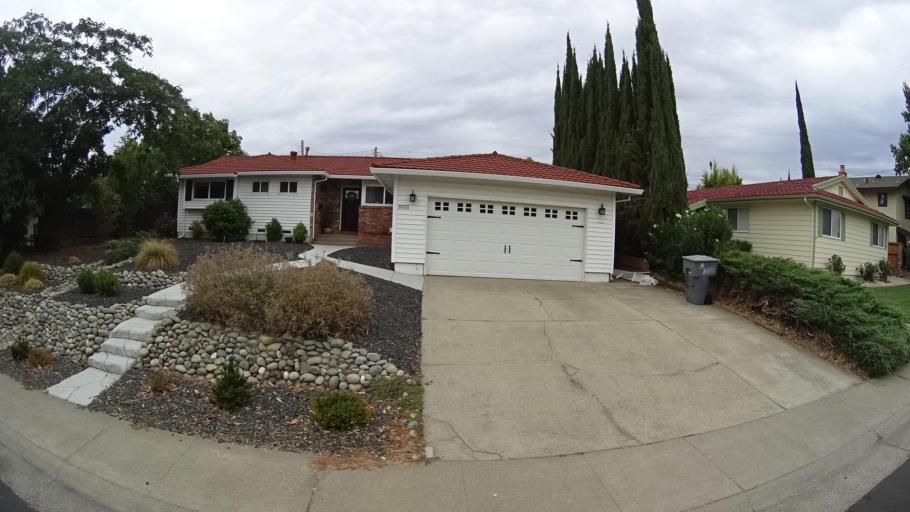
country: US
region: California
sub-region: Placer County
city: Rocklin
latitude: 38.7764
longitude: -121.2461
